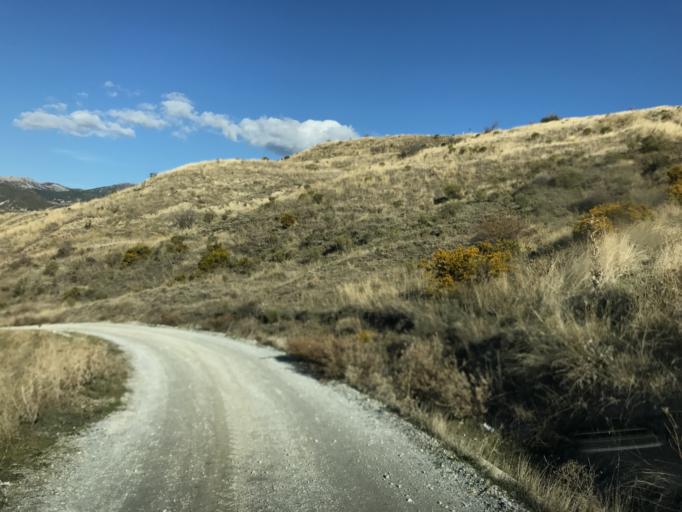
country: ES
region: Andalusia
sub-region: Provincia de Granada
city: Beas de Granada
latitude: 37.2130
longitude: -3.4787
